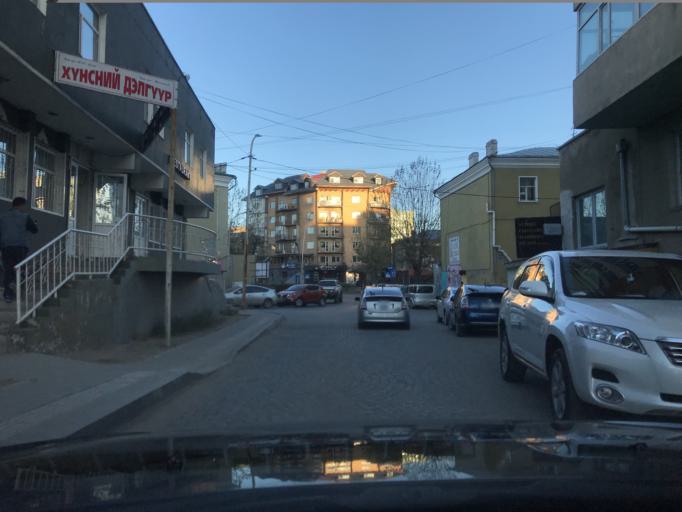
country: MN
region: Ulaanbaatar
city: Ulaanbaatar
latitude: 47.9234
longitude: 106.9094
